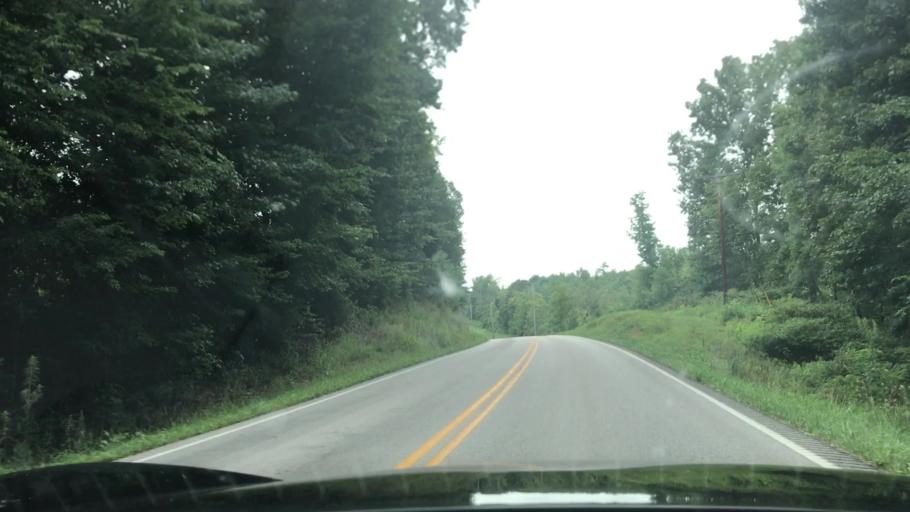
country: US
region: Kentucky
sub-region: Ohio County
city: Oak Grove
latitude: 37.2006
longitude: -86.8870
